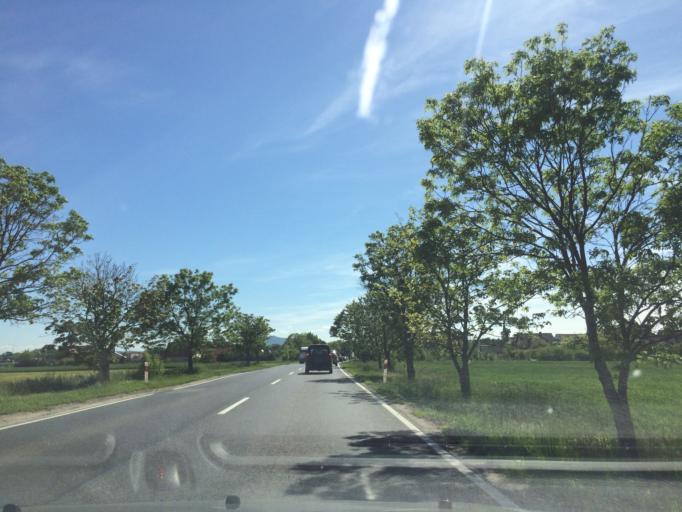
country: PL
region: Lower Silesian Voivodeship
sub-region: Powiat wroclawski
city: Gniechowice
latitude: 50.9920
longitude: 16.8415
